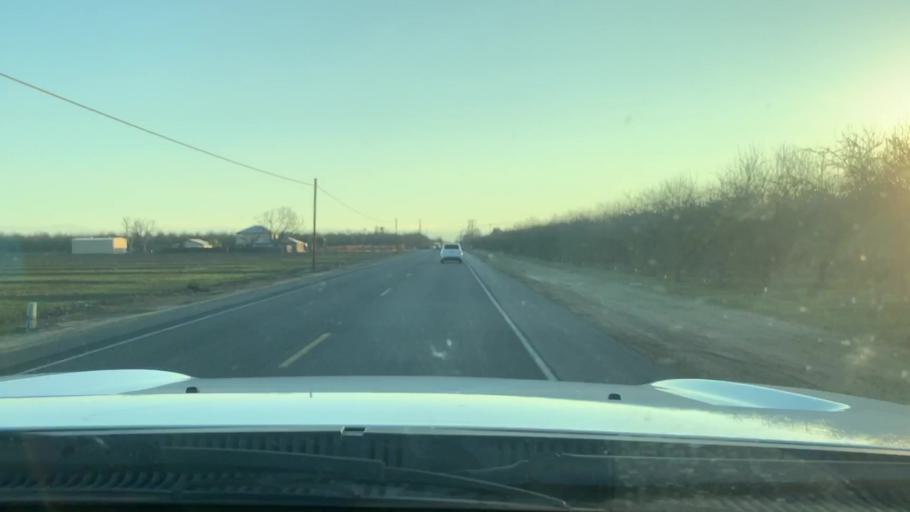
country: US
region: California
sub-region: Kern County
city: Shafter
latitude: 35.5000
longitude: -119.3307
